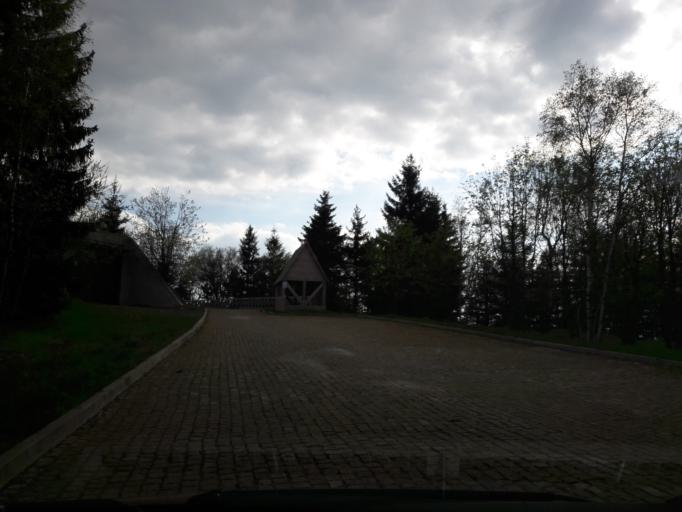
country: CZ
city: Machov
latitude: 50.4779
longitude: 16.2853
